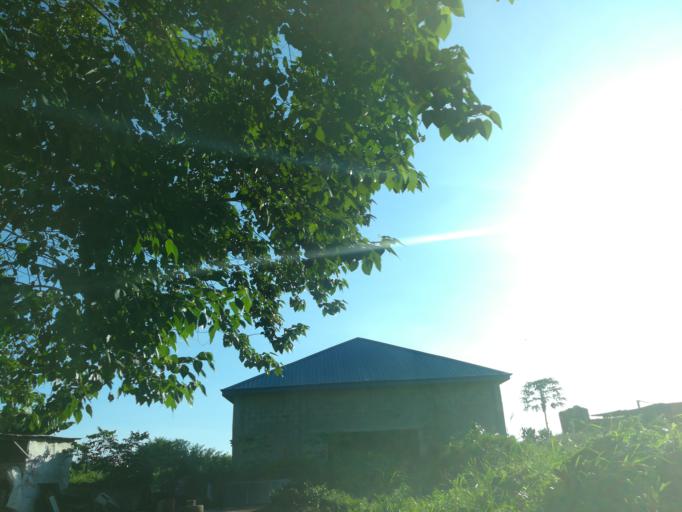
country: NG
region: Lagos
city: Ikorodu
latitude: 6.5693
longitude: 3.5330
